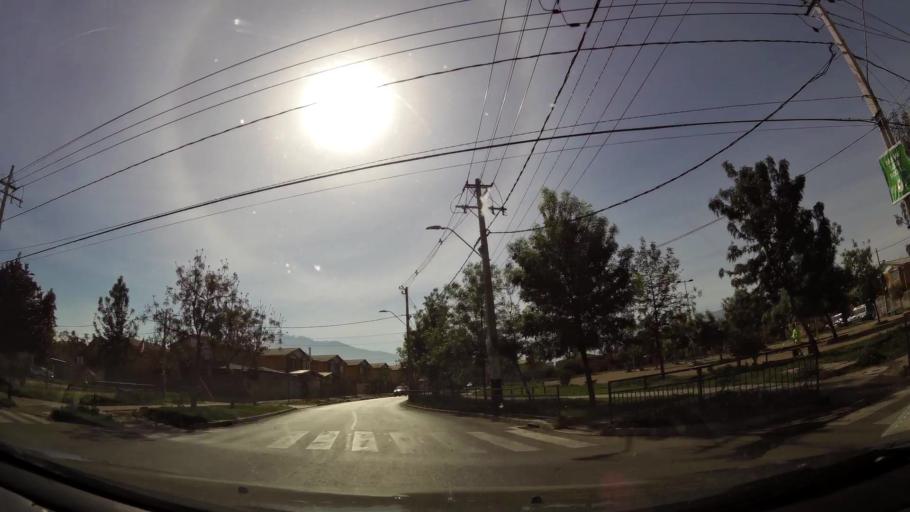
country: CL
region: Santiago Metropolitan
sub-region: Provincia de Cordillera
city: Puente Alto
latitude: -33.6110
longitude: -70.5988
